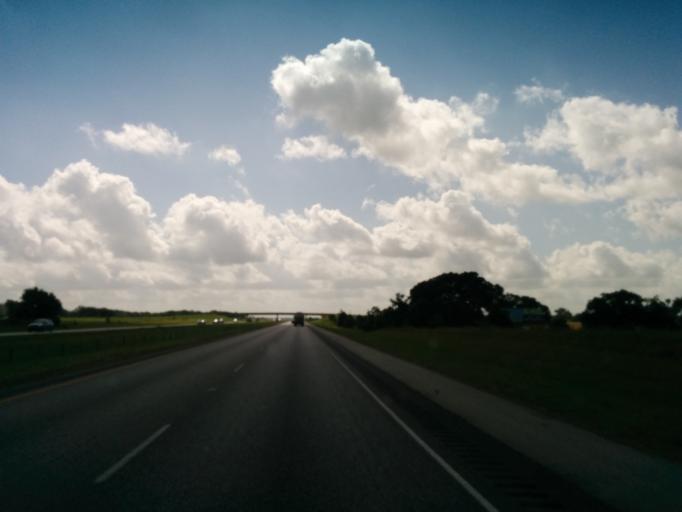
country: US
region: Texas
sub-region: Fayette County
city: Schulenburg
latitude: 29.6903
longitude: -96.9723
